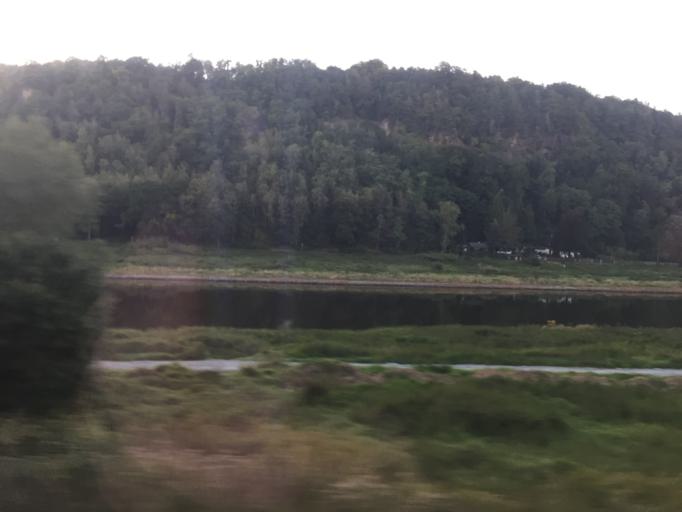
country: DE
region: Saxony
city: Struppen
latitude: 50.9460
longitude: 14.0148
